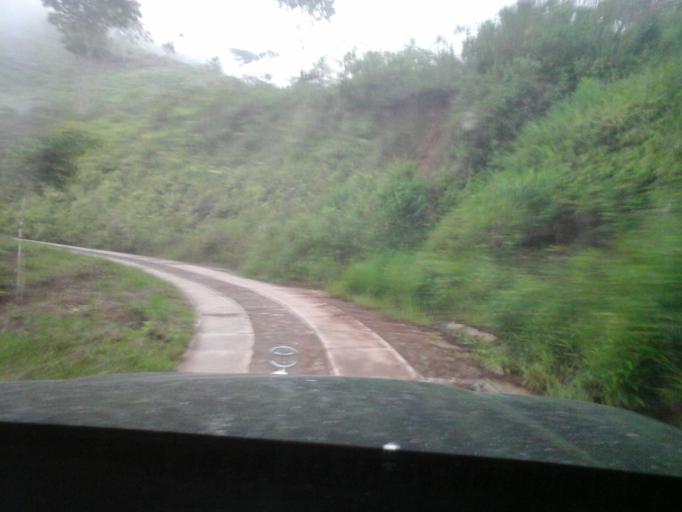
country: CO
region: Cesar
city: Agustin Codazzi
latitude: 9.9422
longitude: -73.1270
